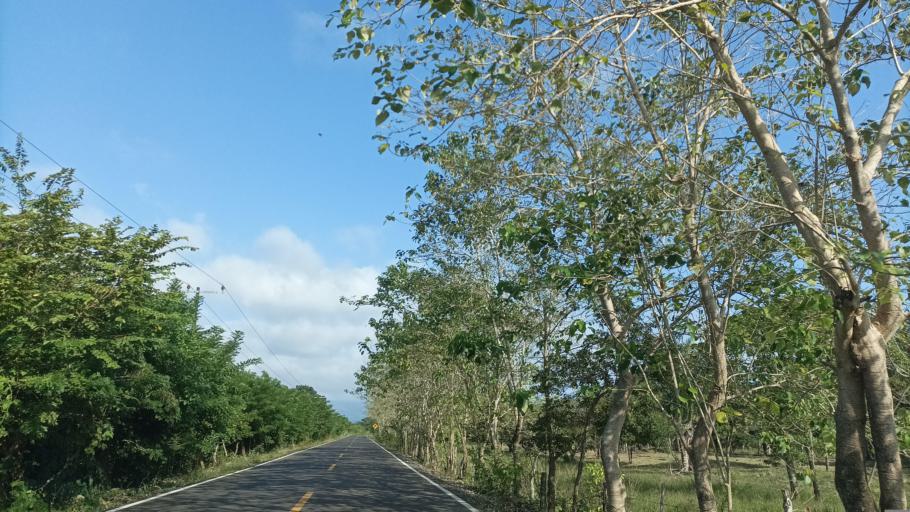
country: MX
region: Veracruz
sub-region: Chinameca
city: Chacalapa
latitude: 18.1535
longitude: -94.6563
